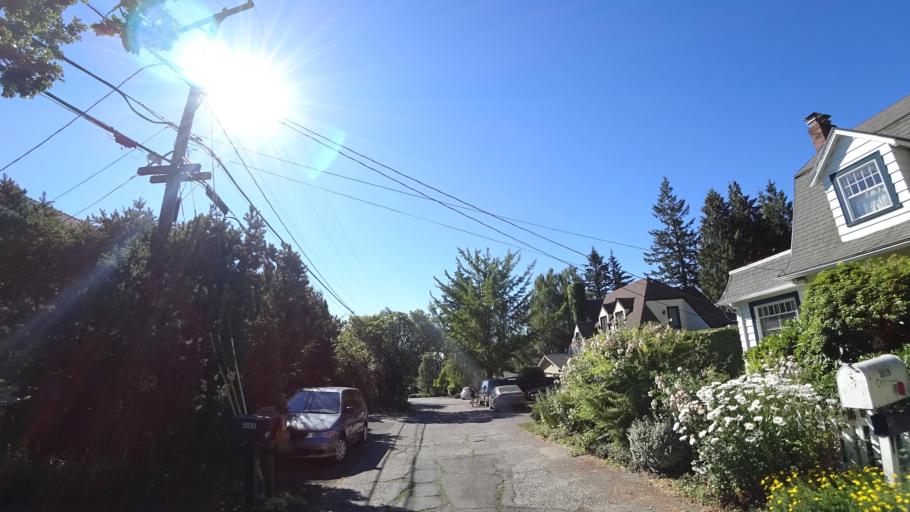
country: US
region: Oregon
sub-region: Multnomah County
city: Portland
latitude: 45.4837
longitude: -122.6873
